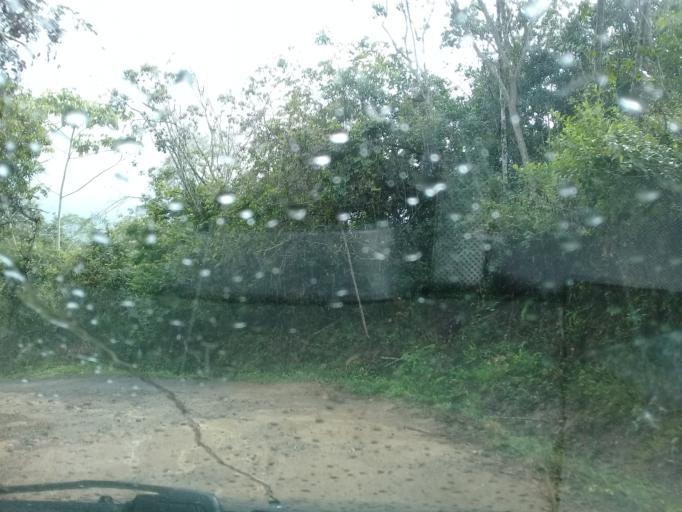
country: CO
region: Cundinamarca
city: Guaduas
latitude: 5.1032
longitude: -74.6092
